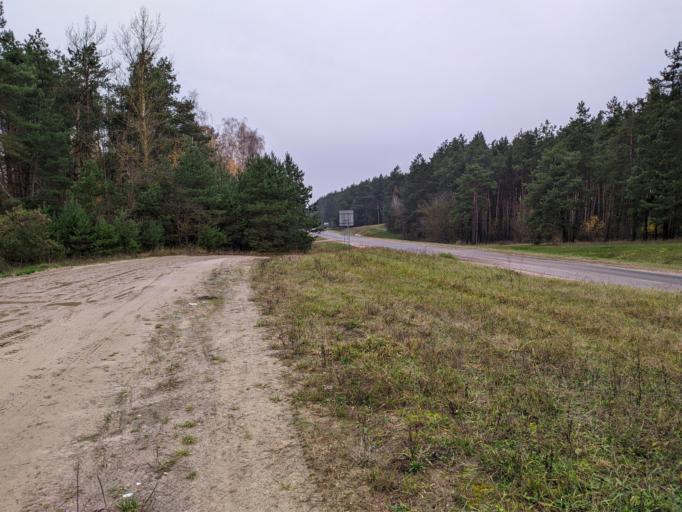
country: BY
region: Brest
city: Kamyanyets
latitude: 52.3908
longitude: 23.8388
